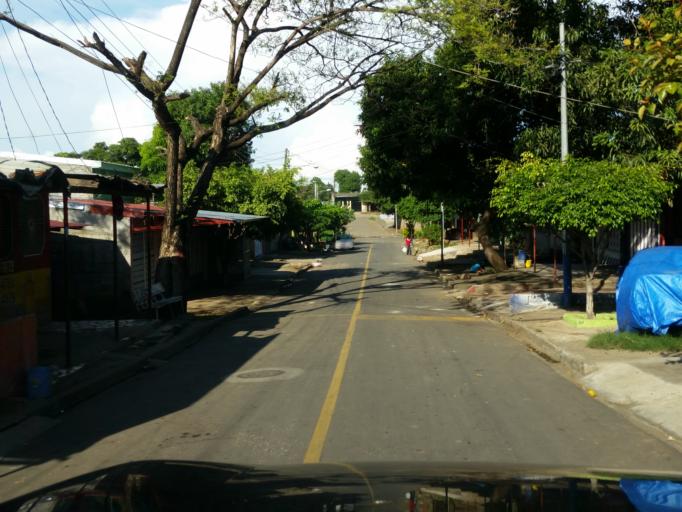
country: NI
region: Managua
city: Managua
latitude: 12.1105
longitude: -86.2298
